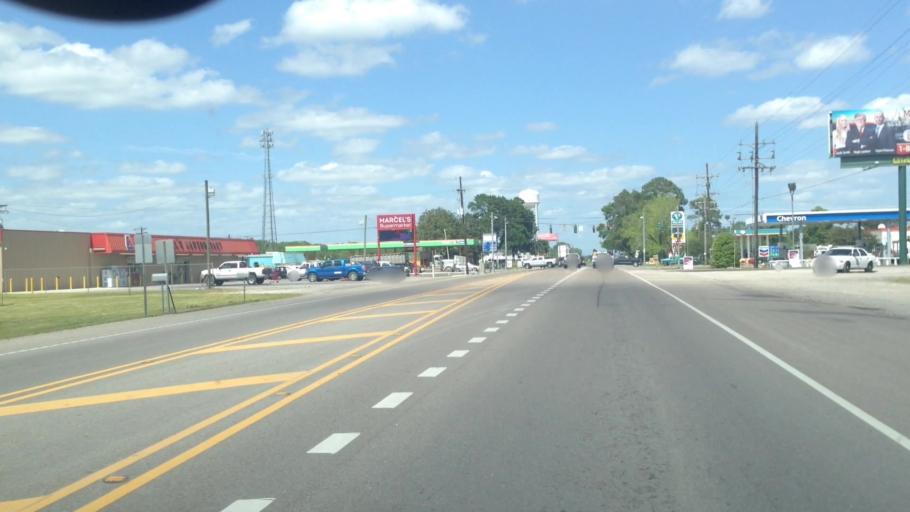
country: US
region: Louisiana
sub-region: Terrebonne Parish
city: Houma
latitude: 29.6442
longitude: -90.6885
